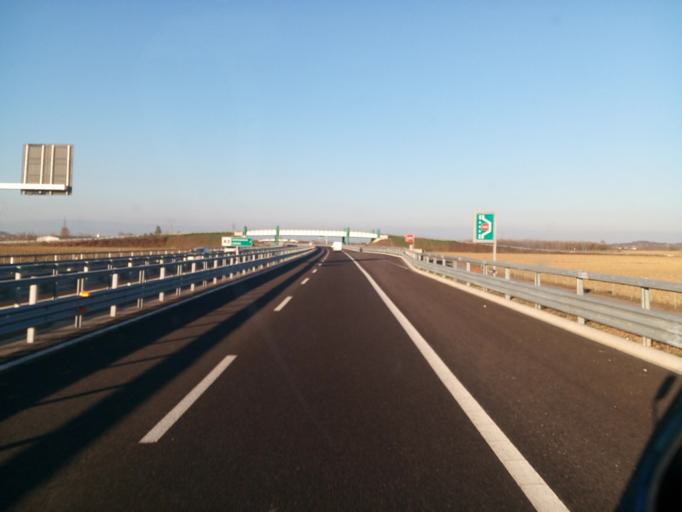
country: IT
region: Veneto
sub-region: Provincia di Vicenza
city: Villaganzerla
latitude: 45.4209
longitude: 11.6358
